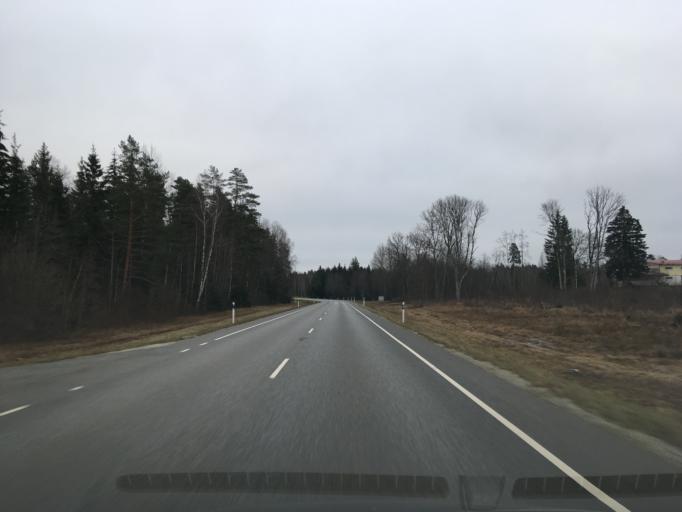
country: EE
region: Laeaene-Virumaa
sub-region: Kadrina vald
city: Kadrina
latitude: 59.4488
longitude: 26.0607
